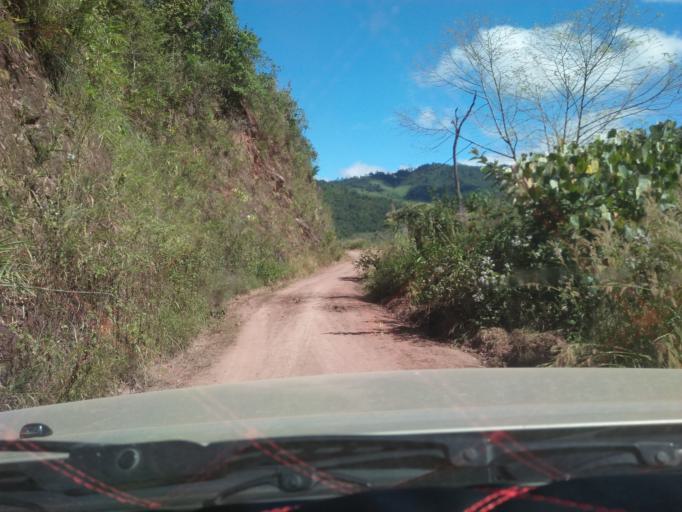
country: TH
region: Nan
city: Chaloem Phra Kiat
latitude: 19.4600
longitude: 101.2748
